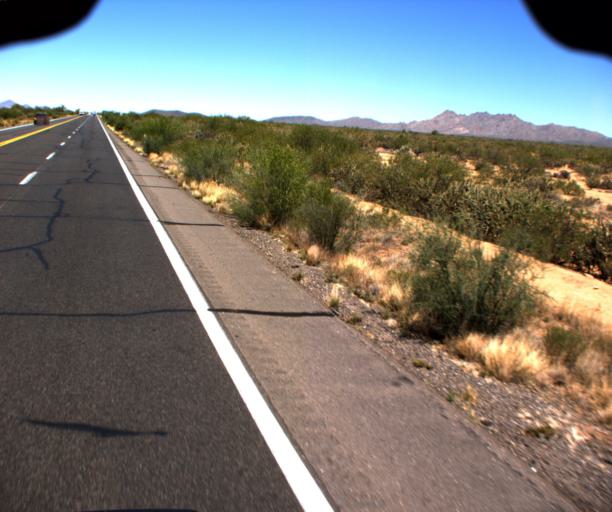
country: US
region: Arizona
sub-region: Yavapai County
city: Congress
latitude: 34.1272
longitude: -112.9559
